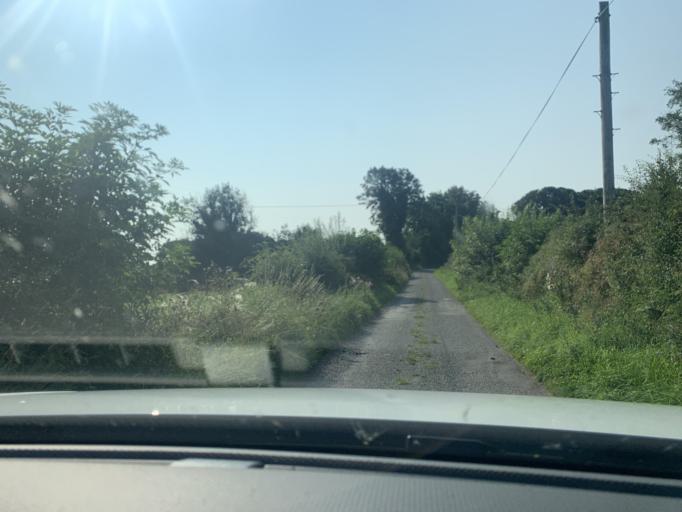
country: IE
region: Connaught
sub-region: Maigh Eo
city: Ballyhaunis
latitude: 53.8000
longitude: -8.7439
